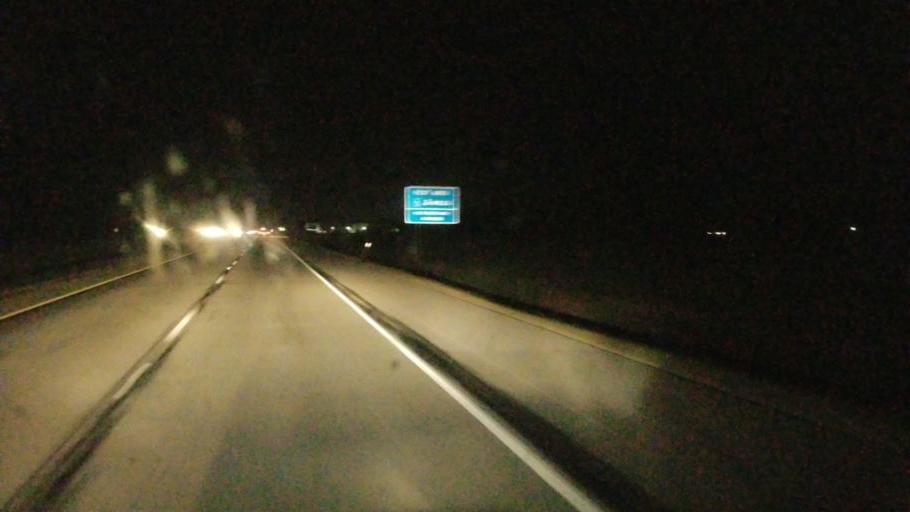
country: US
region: Indiana
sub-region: Allen County
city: Leo-Cedarville
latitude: 41.2613
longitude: -85.0866
